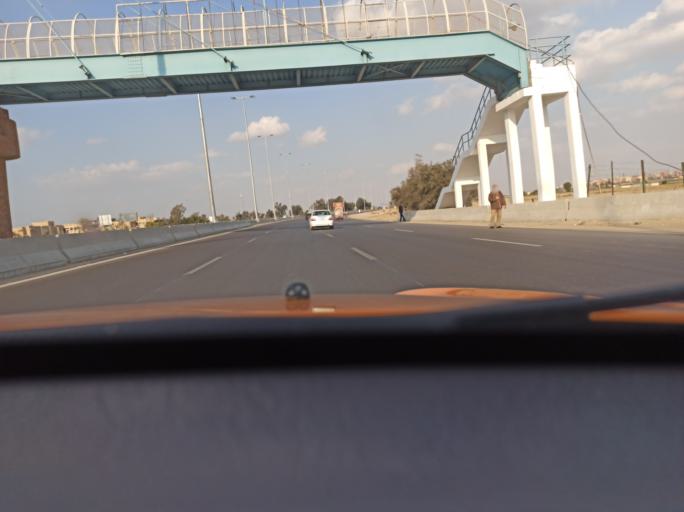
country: EG
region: Al Isma'iliyah
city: Ismailia
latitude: 30.6171
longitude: 32.2283
